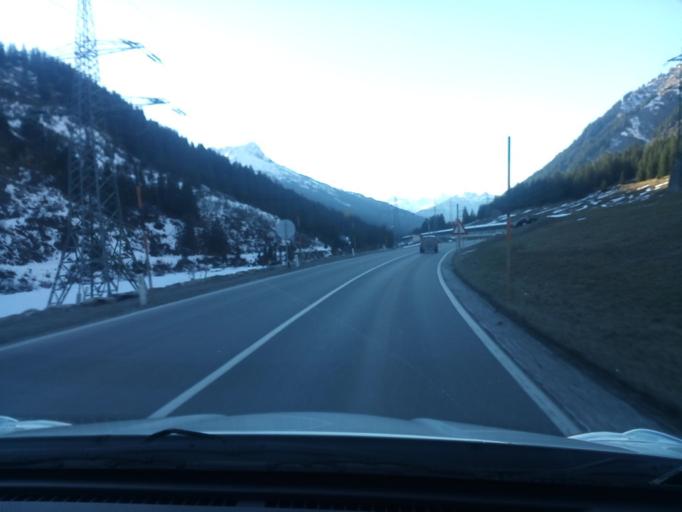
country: AT
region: Vorarlberg
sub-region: Politischer Bezirk Bludenz
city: Klosterle
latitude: 47.1378
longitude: 10.1529
